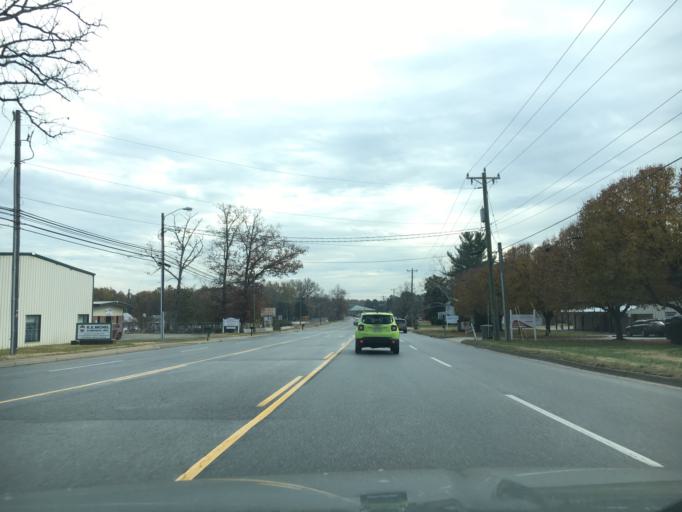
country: US
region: Virginia
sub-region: Prince Edward County
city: Farmville
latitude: 37.3086
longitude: -78.4177
